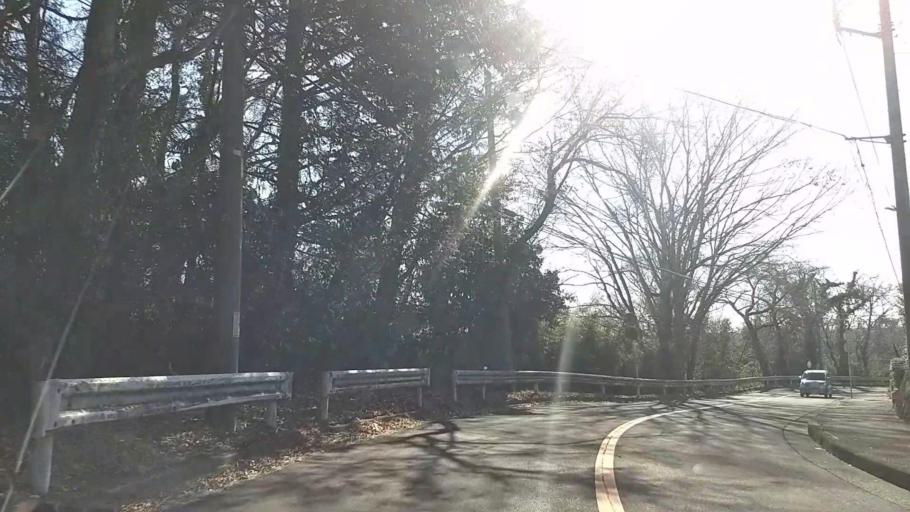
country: JP
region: Kanagawa
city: Hadano
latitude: 35.3847
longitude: 139.2253
